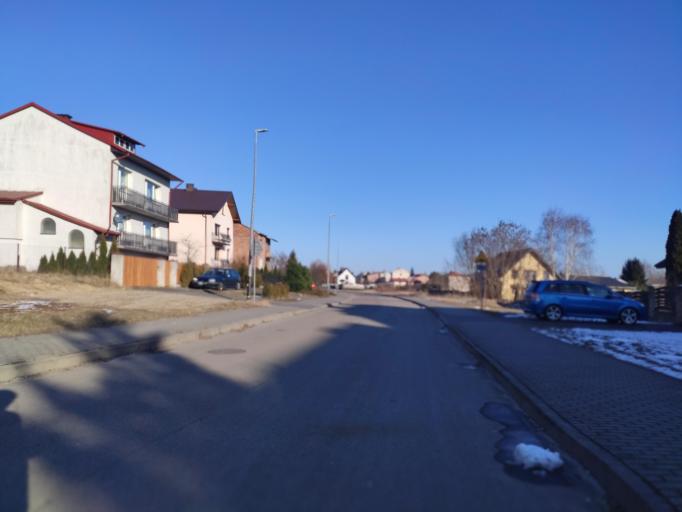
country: PL
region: Lublin Voivodeship
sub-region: Powiat lubartowski
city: Kock
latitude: 51.6388
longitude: 22.4302
